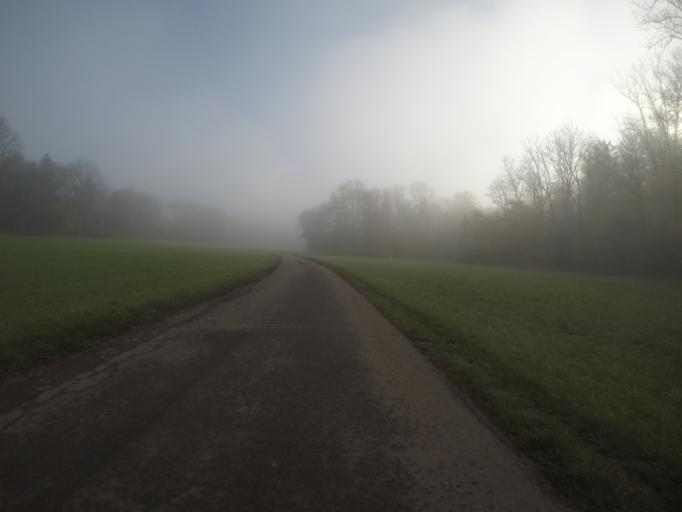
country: DE
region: Baden-Wuerttemberg
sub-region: Regierungsbezirk Stuttgart
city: Ostfildern
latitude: 48.7112
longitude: 9.2332
